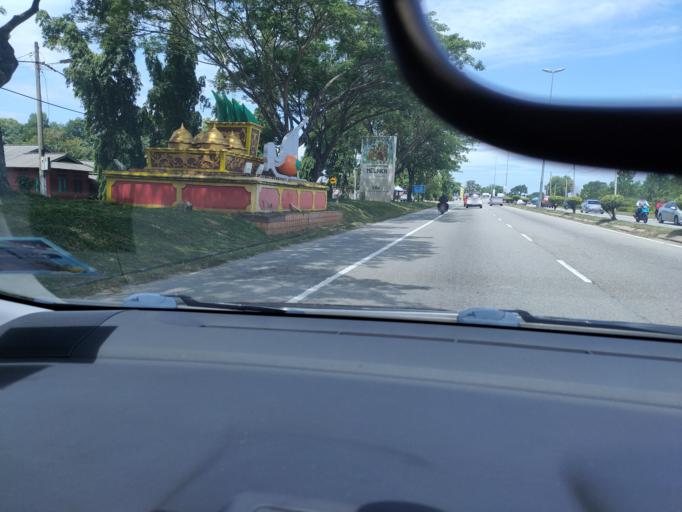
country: MY
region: Melaka
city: Batu Berendam
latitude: 2.2626
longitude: 102.2200
